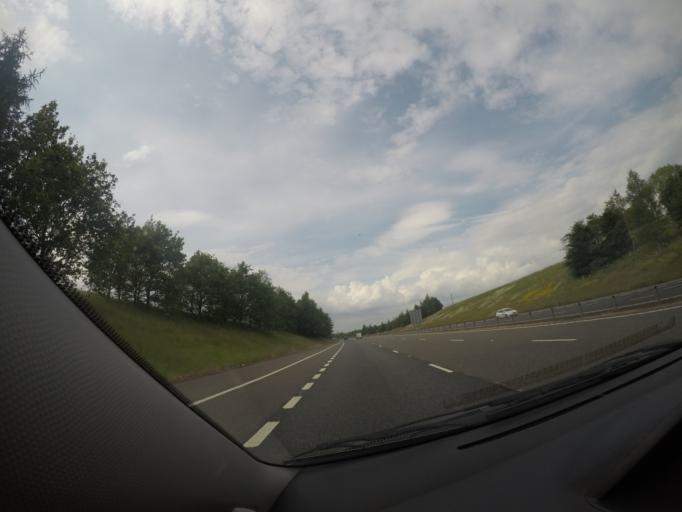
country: GB
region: Scotland
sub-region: Dumfries and Galloway
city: Lockerbie
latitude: 55.1374
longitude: -3.3711
